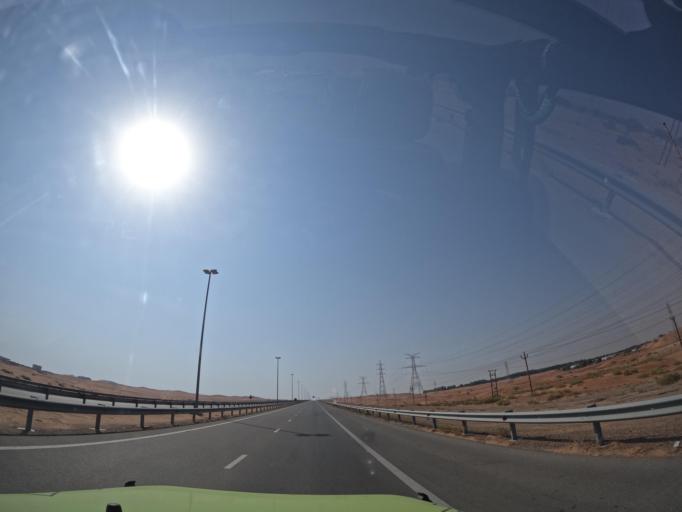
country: OM
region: Al Buraimi
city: Al Buraymi
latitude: 24.3555
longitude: 55.7343
